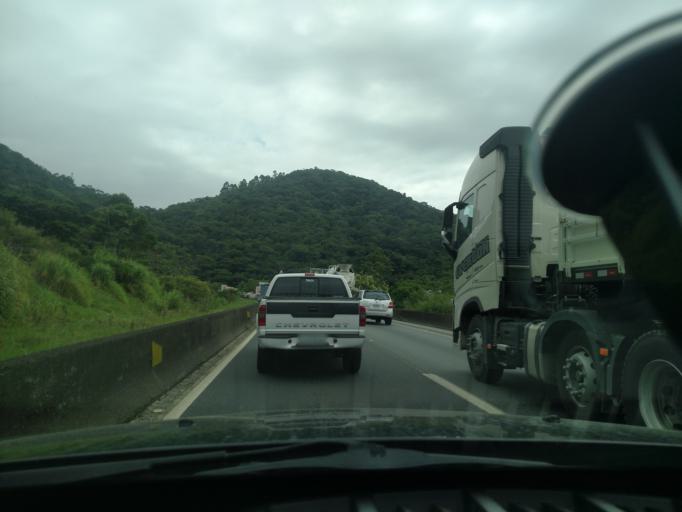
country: BR
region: Santa Catarina
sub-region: Itapema
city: Itapema
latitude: -27.0512
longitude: -48.5978
